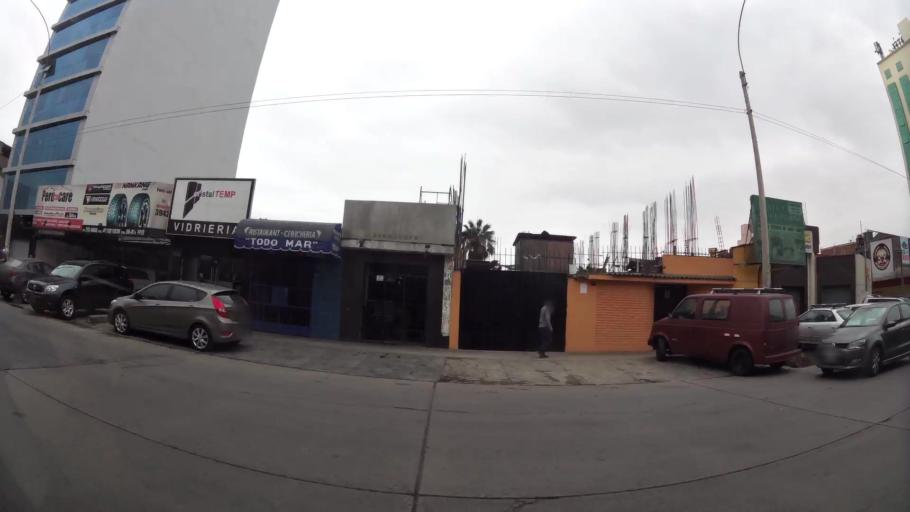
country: PE
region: Lima
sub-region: Lima
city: Surco
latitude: -12.1149
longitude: -76.9998
